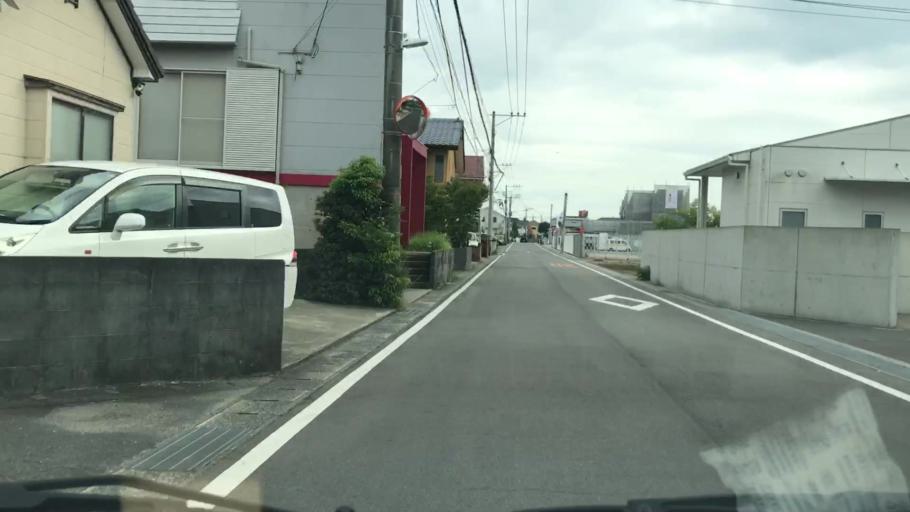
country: JP
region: Saga Prefecture
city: Saga-shi
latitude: 33.2759
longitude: 130.2636
